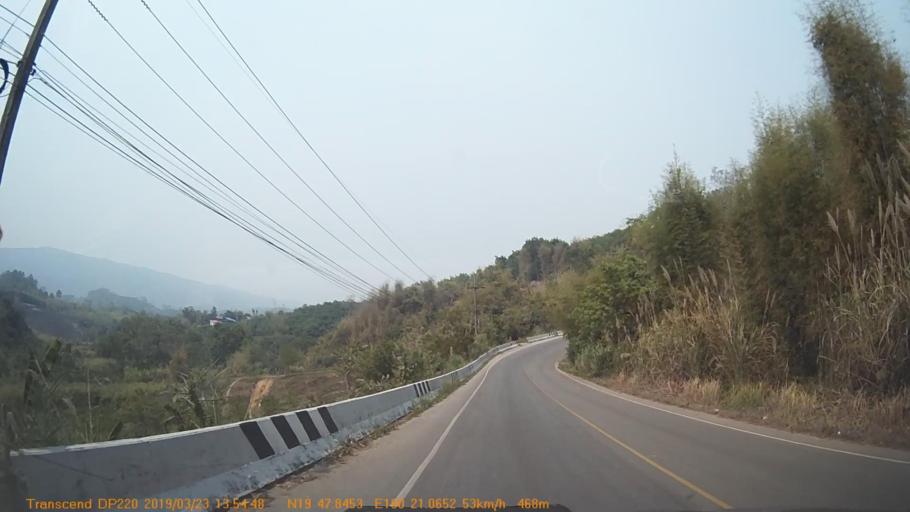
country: TH
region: Chiang Rai
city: Khun Tan
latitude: 19.7978
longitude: 100.3512
